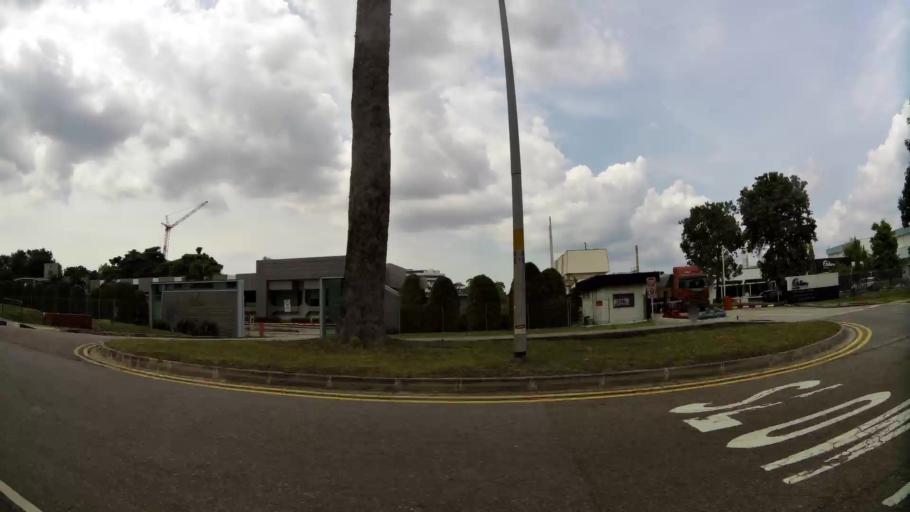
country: MY
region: Johor
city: Johor Bahru
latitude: 1.3297
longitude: 103.7081
